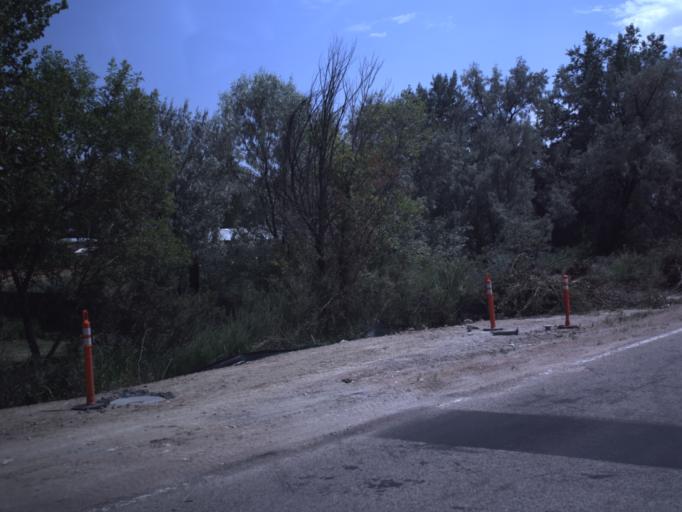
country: US
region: Utah
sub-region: Duchesne County
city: Roosevelt
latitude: 40.4318
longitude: -110.0301
